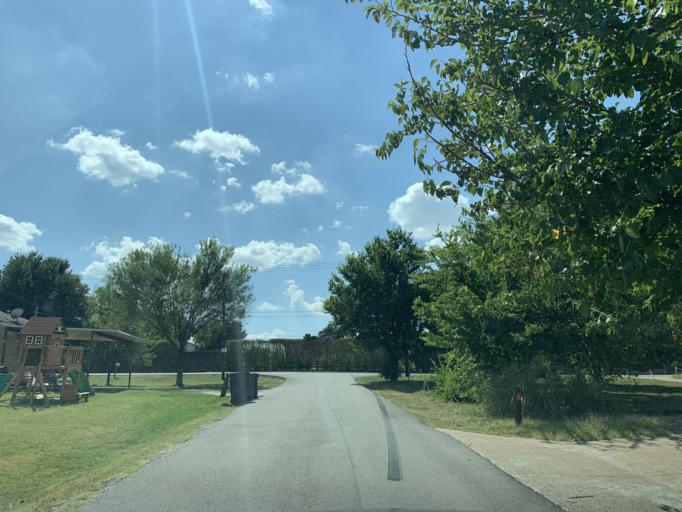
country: US
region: Texas
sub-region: Dallas County
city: DeSoto
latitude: 32.6648
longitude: -96.8207
